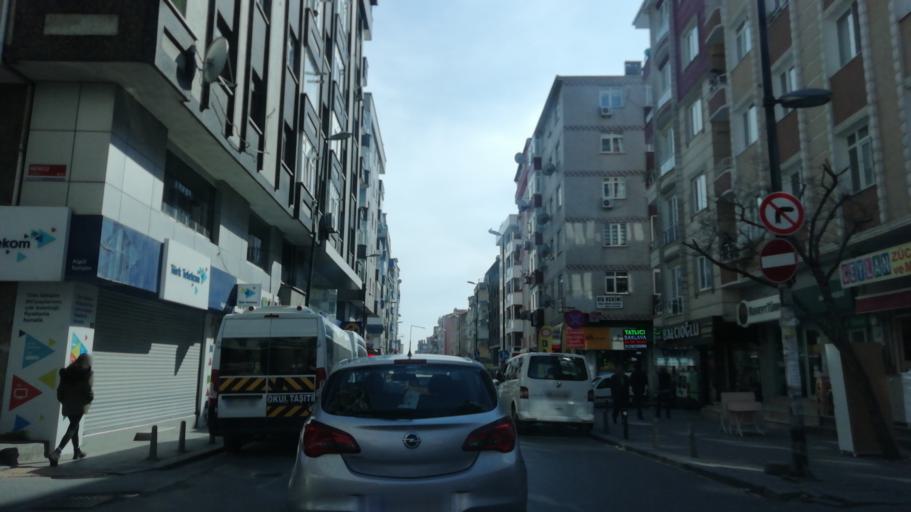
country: TR
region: Istanbul
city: Bahcelievler
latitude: 40.9983
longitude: 28.8385
